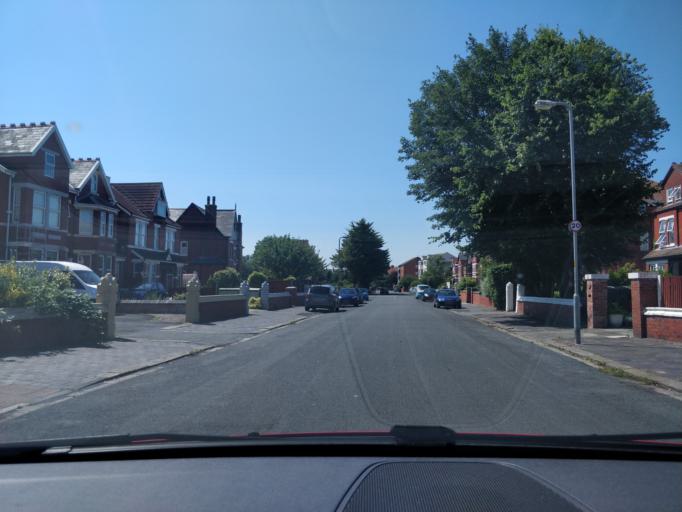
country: GB
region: England
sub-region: Sefton
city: Southport
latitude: 53.6585
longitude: -2.9967
